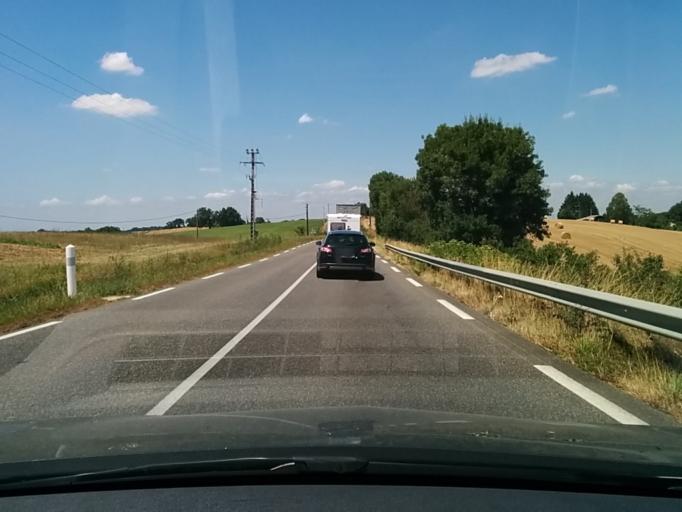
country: FR
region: Midi-Pyrenees
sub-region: Departement du Gers
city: Eauze
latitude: 43.7741
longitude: 0.1247
